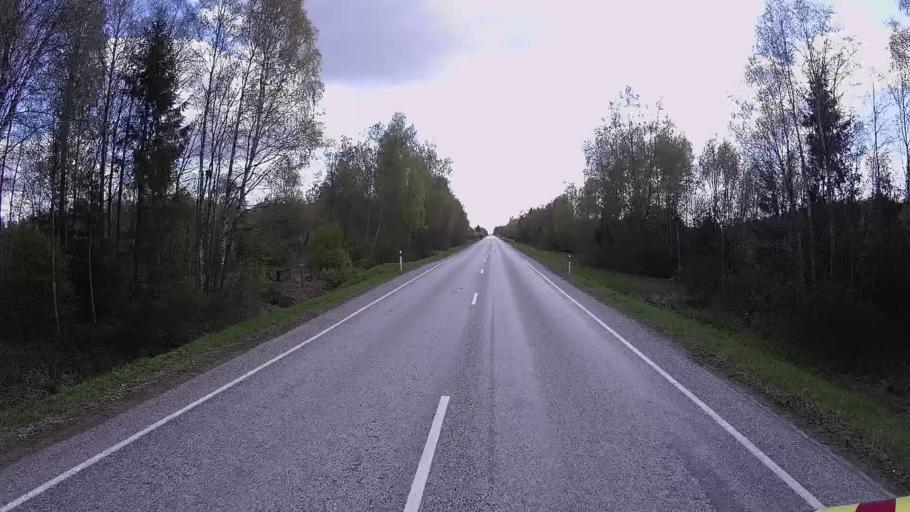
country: EE
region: Jogevamaa
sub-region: Jogeva linn
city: Jogeva
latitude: 58.7730
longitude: 26.4642
